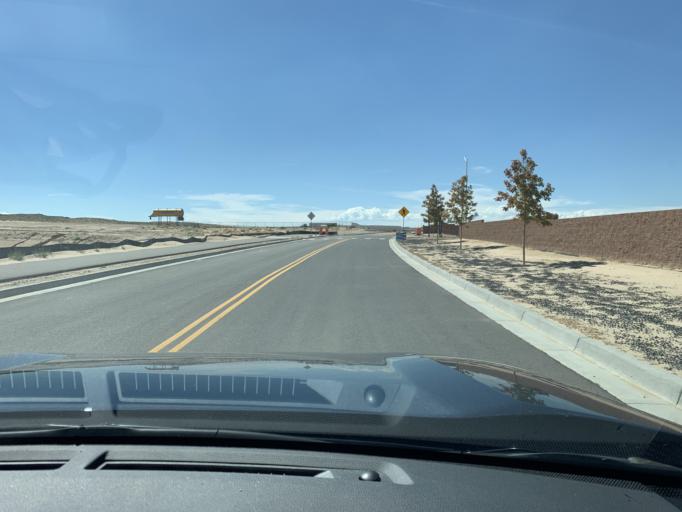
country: US
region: New Mexico
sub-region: Valencia County
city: Los Lunas
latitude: 34.8185
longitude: -106.8003
